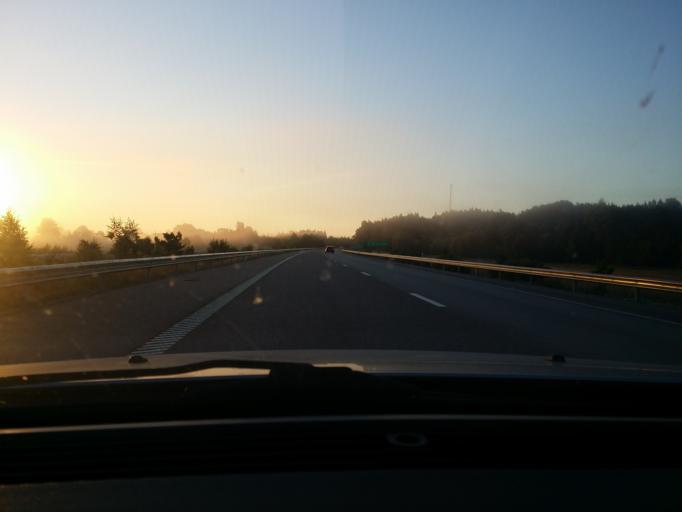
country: SE
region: Uppsala
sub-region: Enkopings Kommun
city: Grillby
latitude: 59.6395
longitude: 17.2491
